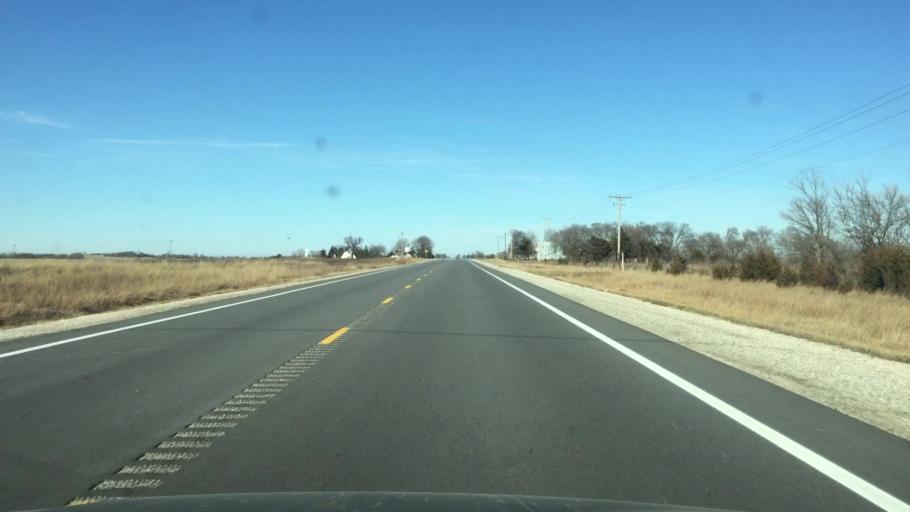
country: US
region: Kansas
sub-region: Anderson County
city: Garnett
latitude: 38.3639
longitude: -95.2485
